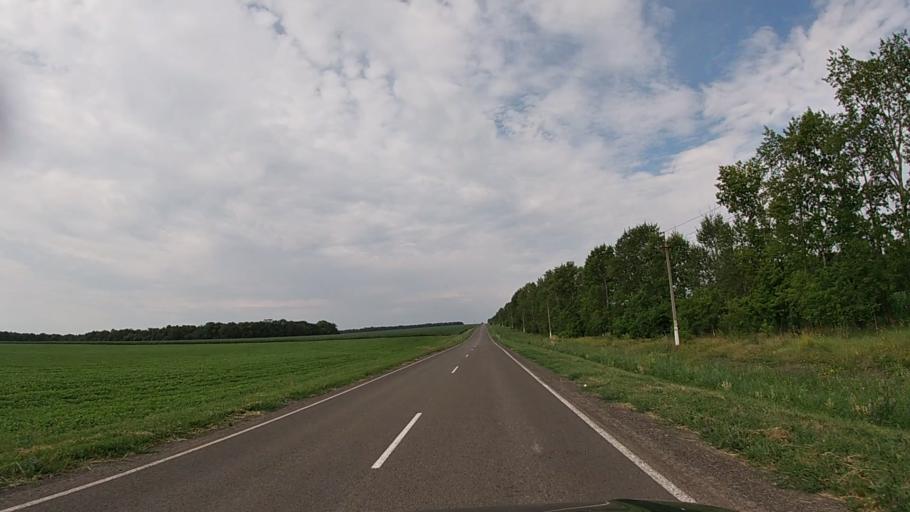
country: RU
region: Belgorod
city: Krasnaya Yaruga
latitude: 50.8296
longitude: 35.4769
